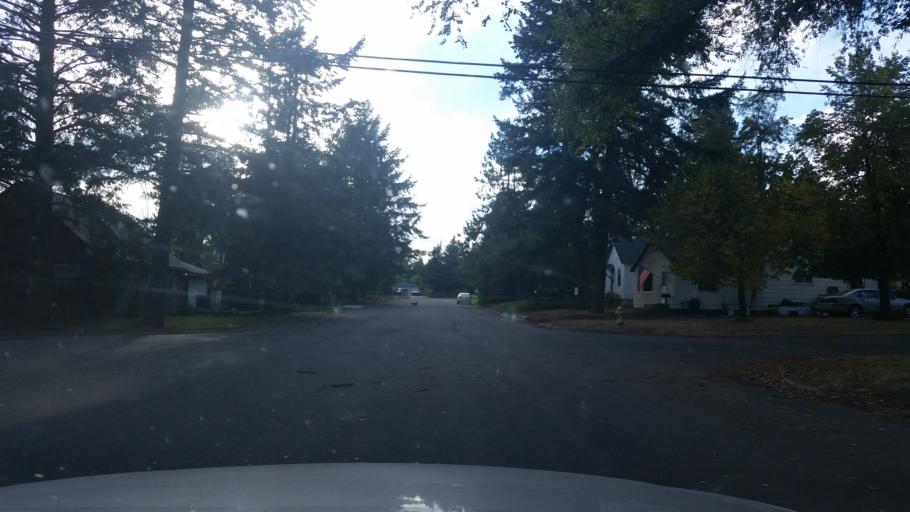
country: US
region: Washington
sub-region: Spokane County
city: Cheney
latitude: 47.4826
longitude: -117.5879
